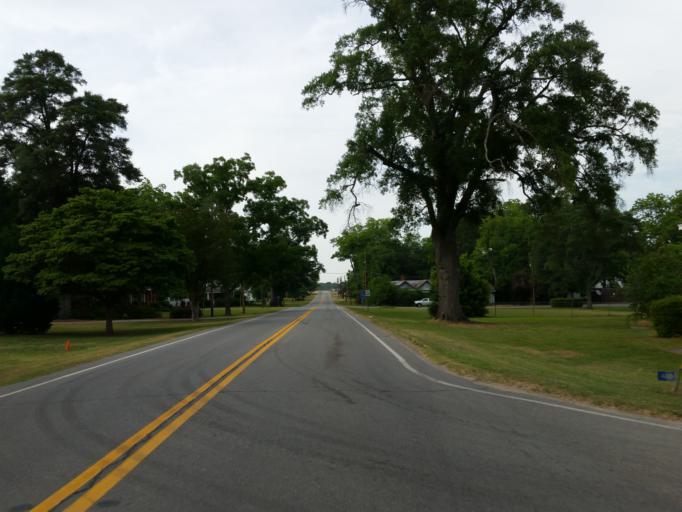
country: US
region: Georgia
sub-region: Dooly County
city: Unadilla
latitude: 32.1943
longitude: -83.7633
